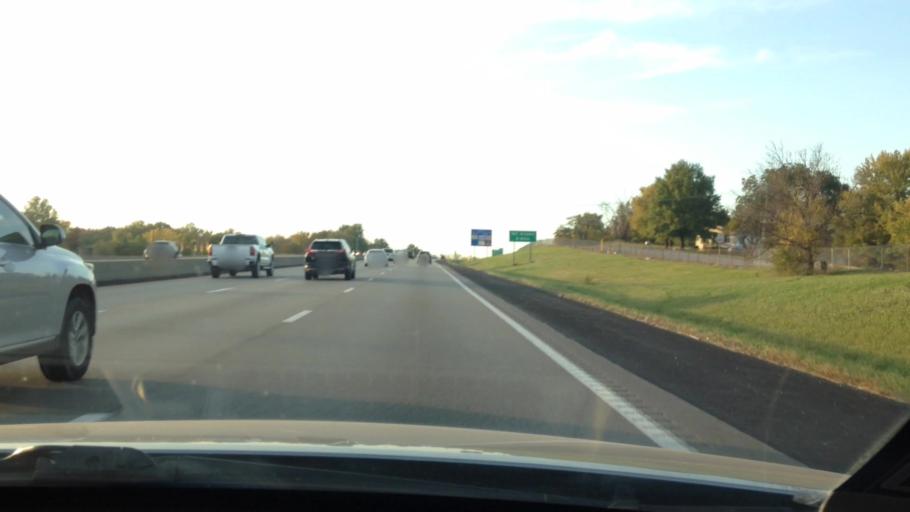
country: US
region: Missouri
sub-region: Platte County
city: Riverside
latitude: 39.2031
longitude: -94.6306
